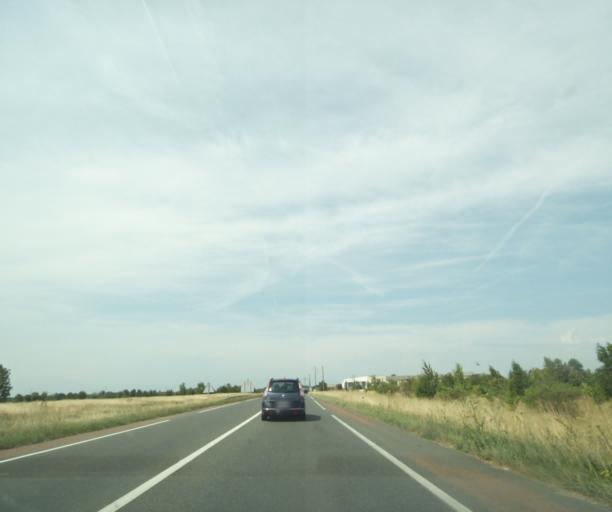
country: FR
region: Centre
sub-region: Departement d'Indre-et-Loire
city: Sorigny
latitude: 47.2575
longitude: 0.7012
